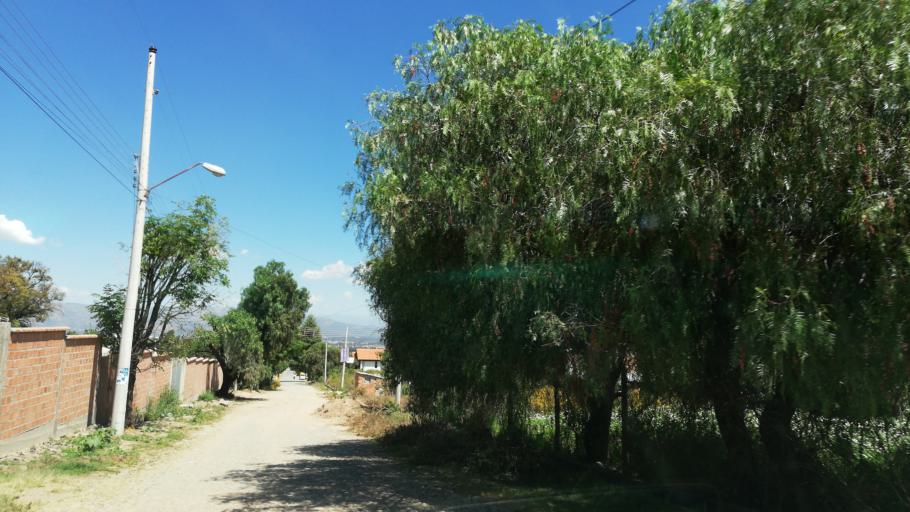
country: BO
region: Cochabamba
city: Cochabamba
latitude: -17.3276
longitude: -66.2144
